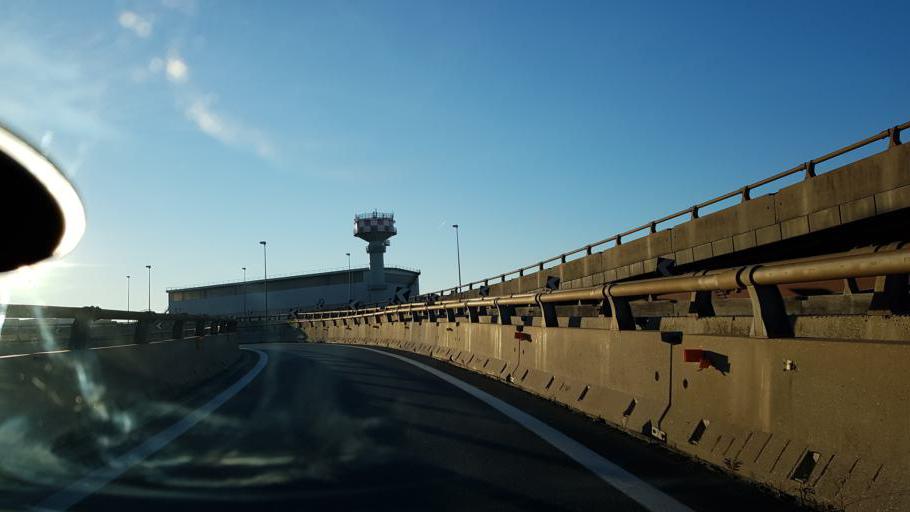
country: IT
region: Liguria
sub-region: Provincia di Genova
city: San Teodoro
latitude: 44.4167
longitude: 8.8593
